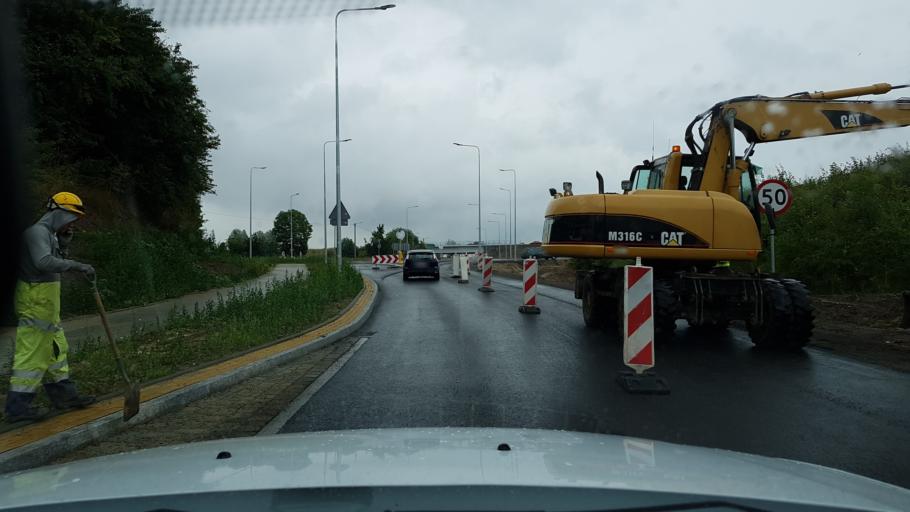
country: PL
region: West Pomeranian Voivodeship
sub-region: Powiat goleniowski
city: Maszewo
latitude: 53.4356
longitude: 15.0744
